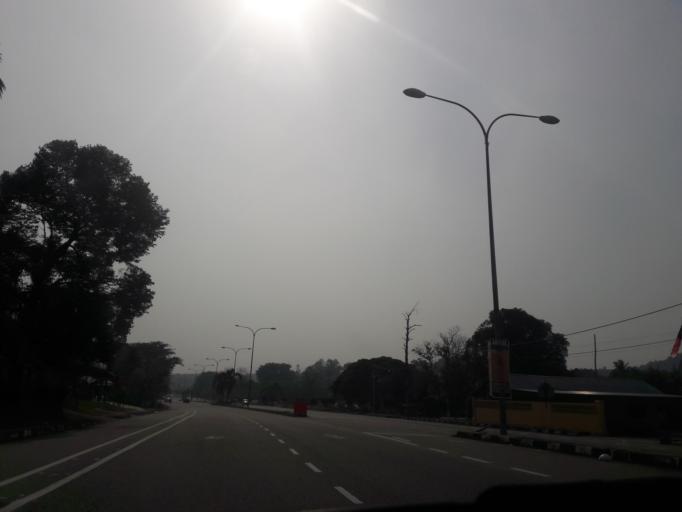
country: MY
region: Kedah
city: Kulim
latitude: 5.3542
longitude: 100.5356
